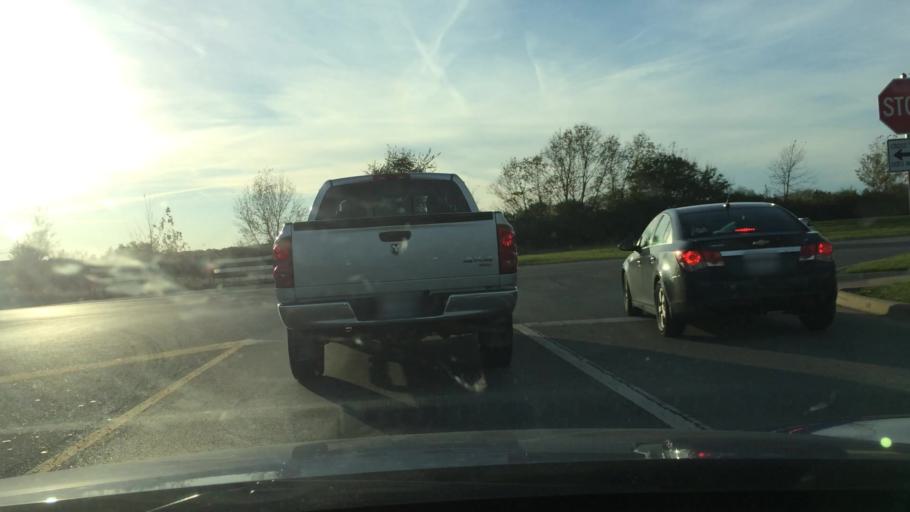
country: US
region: Ohio
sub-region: Franklin County
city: Hilliard
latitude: 40.0743
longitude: -83.1496
